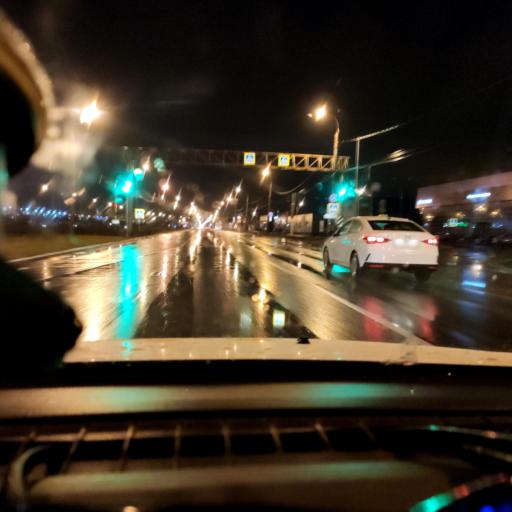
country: RU
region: Samara
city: Samara
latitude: 53.1374
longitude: 50.1766
